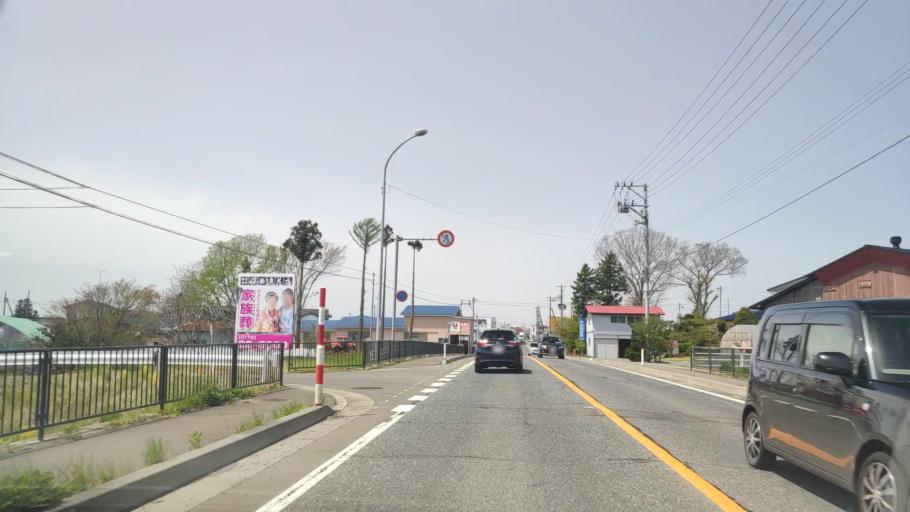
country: JP
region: Aomori
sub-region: Misawa Shi
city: Inuotose
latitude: 40.6064
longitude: 141.2898
